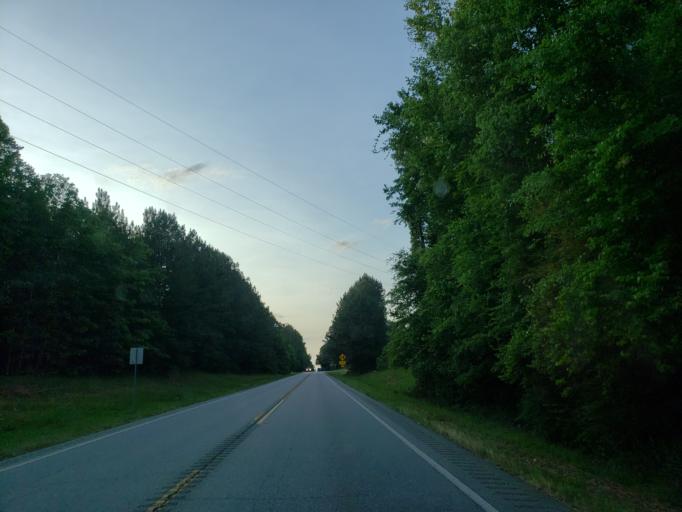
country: US
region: Georgia
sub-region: Coweta County
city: Newnan
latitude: 33.4445
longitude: -84.8791
